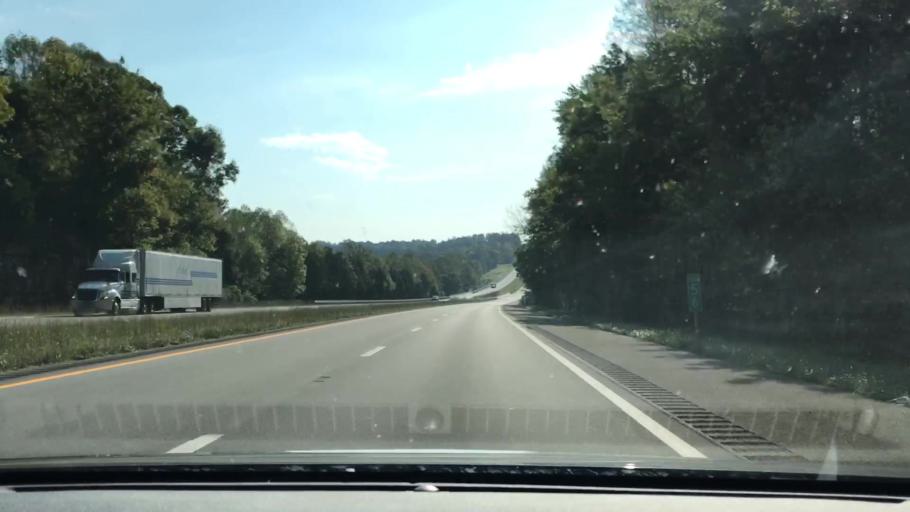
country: US
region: Kentucky
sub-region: Russell County
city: Russell Springs
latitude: 37.0610
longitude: -85.1815
